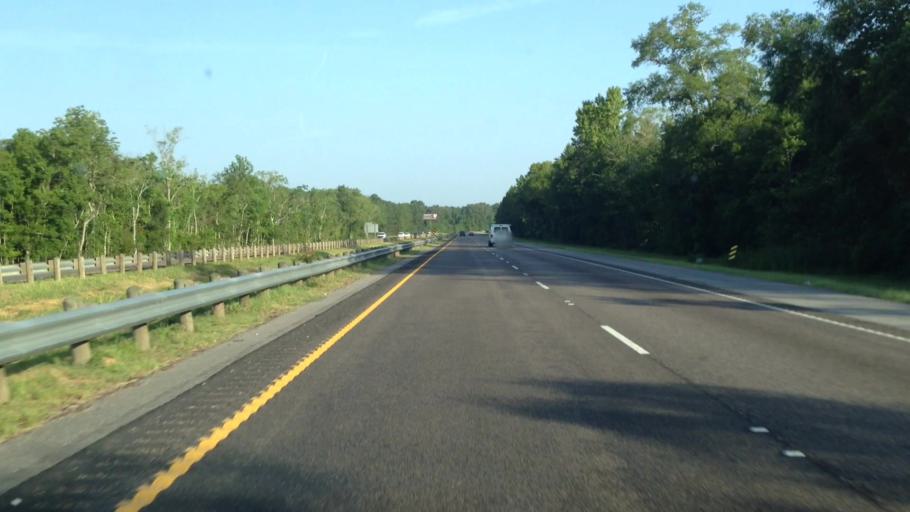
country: US
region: Louisiana
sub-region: Tangipahoa Parish
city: Ponchatoula
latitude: 30.4192
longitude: -90.4440
